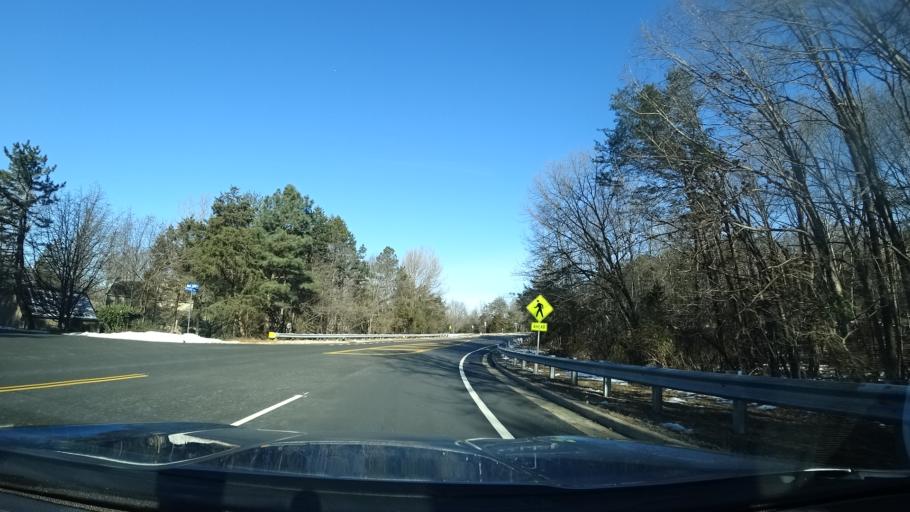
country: US
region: Virginia
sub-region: Fairfax County
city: Reston
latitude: 38.9724
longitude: -77.3577
